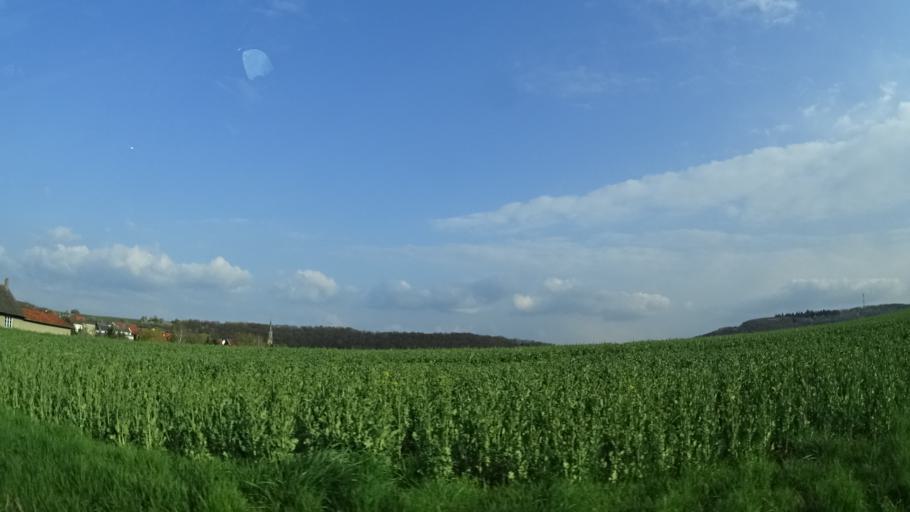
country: DE
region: Rheinland-Pfalz
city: Sponheim
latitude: 49.8439
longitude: 7.7201
